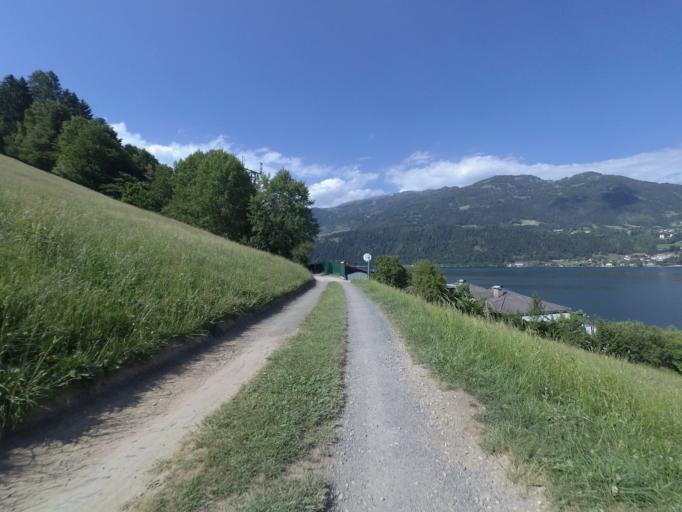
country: AT
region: Carinthia
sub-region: Politischer Bezirk Spittal an der Drau
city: Millstatt
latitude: 46.7807
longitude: 13.5934
